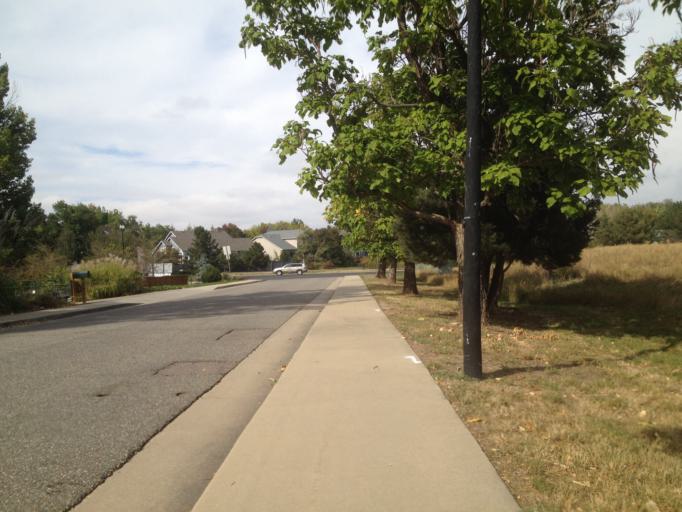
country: US
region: Colorado
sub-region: Boulder County
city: Louisville
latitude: 39.9994
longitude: -105.1278
